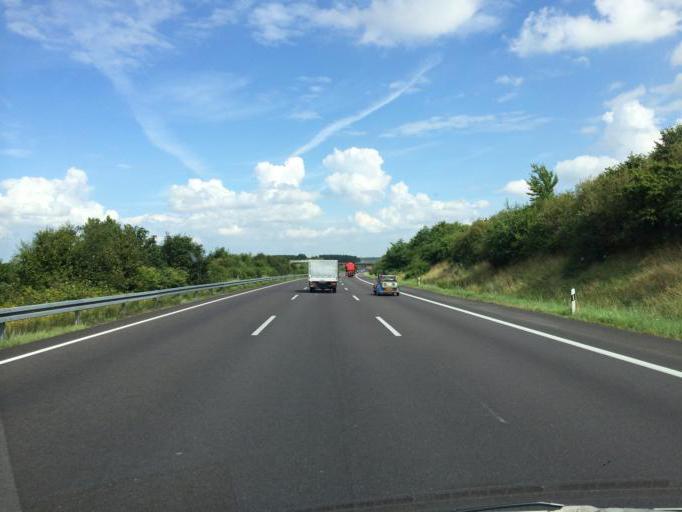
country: DE
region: Lower Saxony
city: Konigslutter am Elm
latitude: 52.3136
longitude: 10.7811
